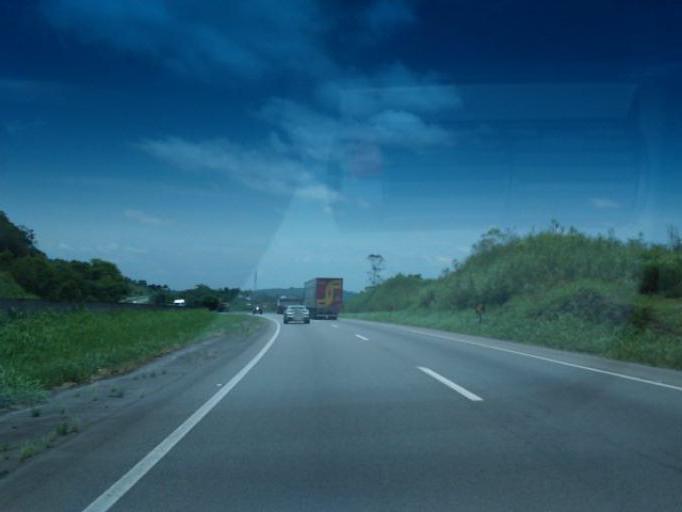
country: BR
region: Sao Paulo
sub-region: Miracatu
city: Miracatu
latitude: -24.3070
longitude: -47.4982
